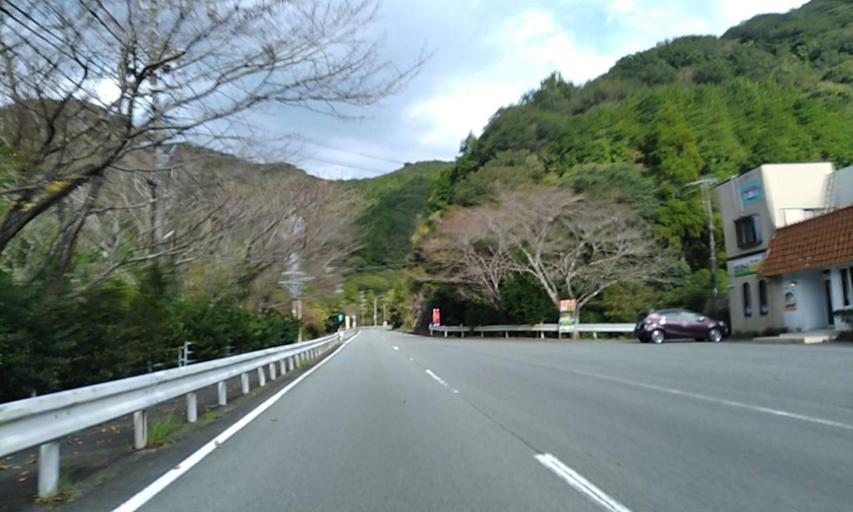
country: JP
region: Mie
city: Ise
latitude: 34.2571
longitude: 136.4734
